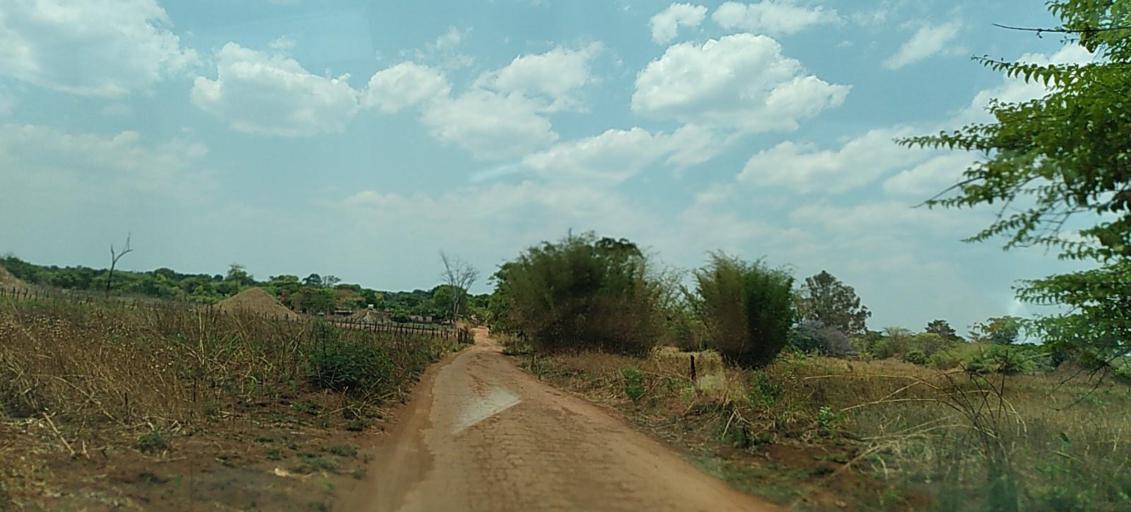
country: ZM
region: Copperbelt
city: Chingola
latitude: -12.5425
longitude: 27.6322
